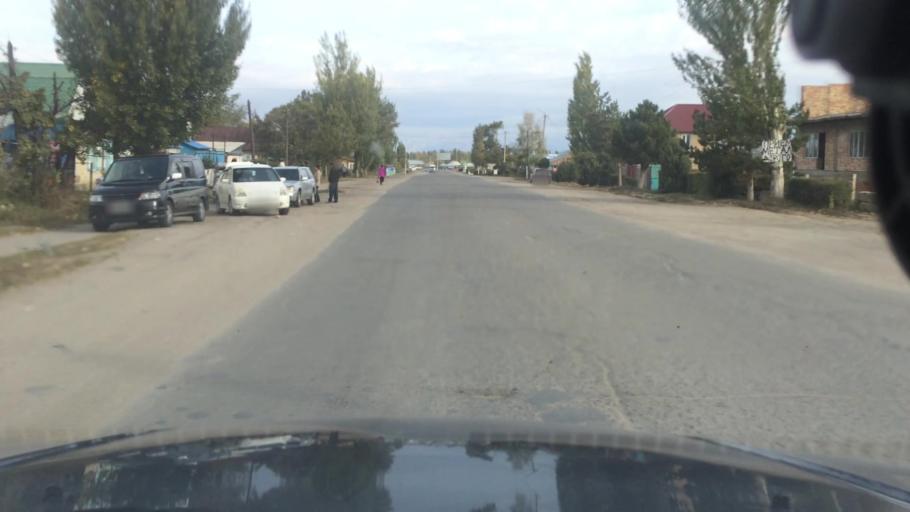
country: KG
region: Ysyk-Koel
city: Karakol
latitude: 42.5197
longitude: 78.3858
